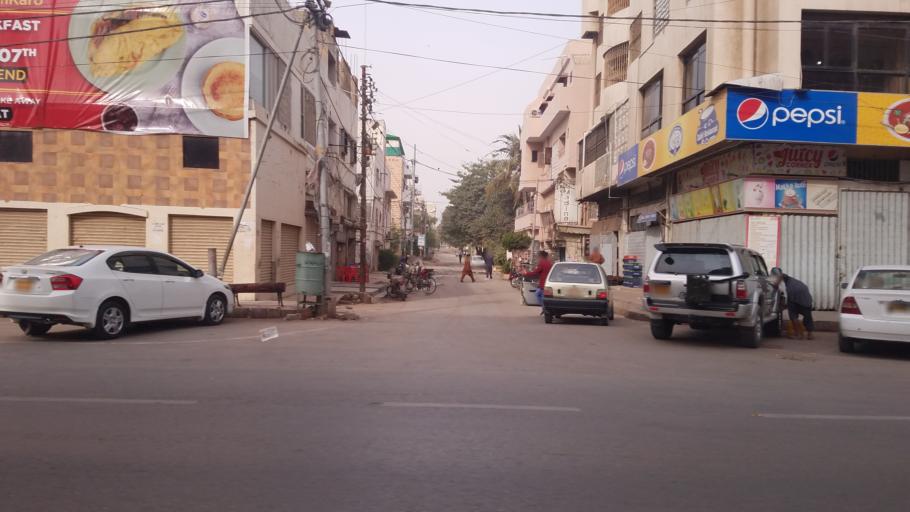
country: PK
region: Sindh
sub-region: Karachi District
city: Karachi
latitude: 24.8685
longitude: 67.0577
